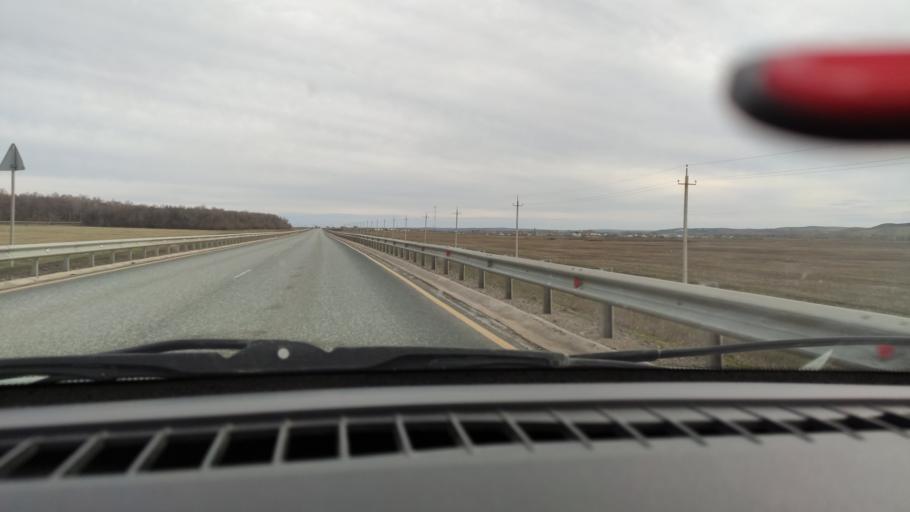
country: RU
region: Bashkortostan
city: Yermolayevo
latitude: 52.5002
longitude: 55.8294
